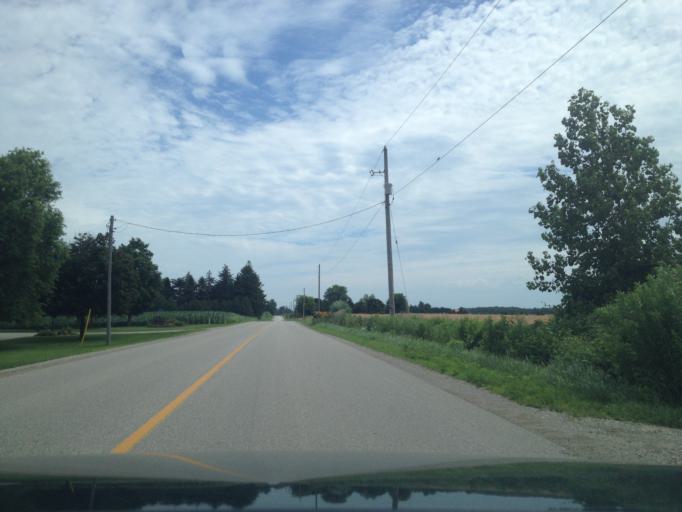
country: CA
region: Ontario
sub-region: Oxford County
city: Woodstock
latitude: 42.9931
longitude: -80.6588
